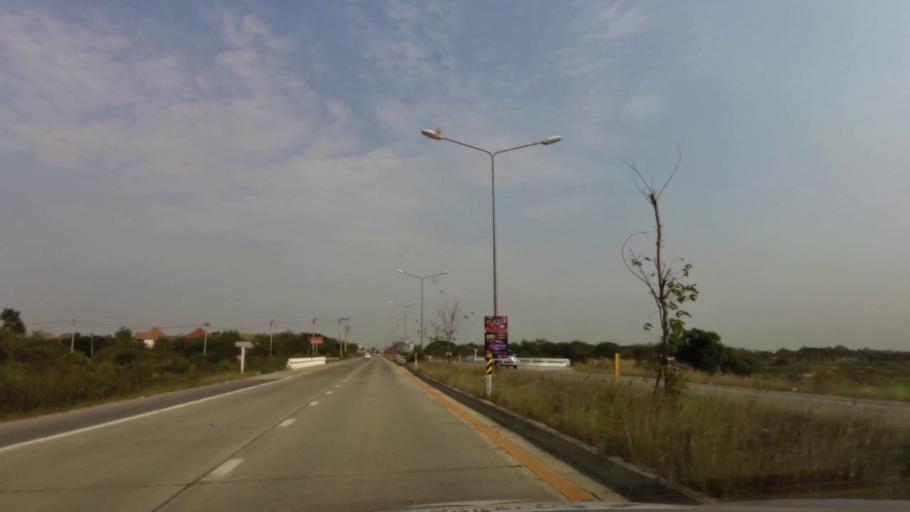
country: TH
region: Phra Nakhon Si Ayutthaya
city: Phra Nakhon Si Ayutthaya
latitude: 14.3332
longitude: 100.5971
